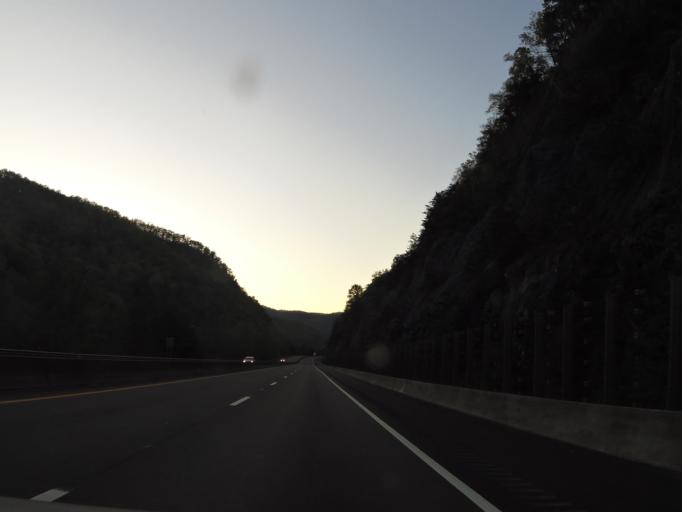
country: US
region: Tennessee
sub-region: Cocke County
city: Newport
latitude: 35.8021
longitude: -83.1322
